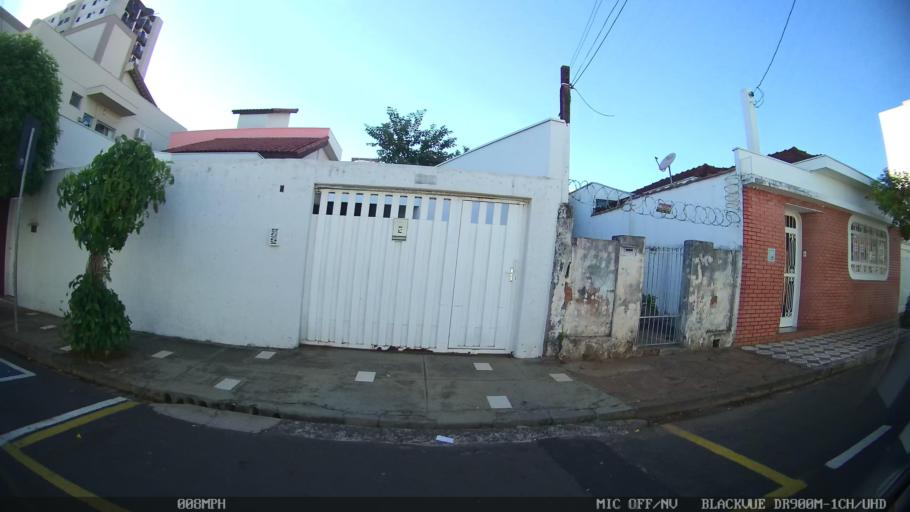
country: BR
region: Sao Paulo
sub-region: Franca
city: Franca
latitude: -20.5326
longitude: -47.4017
